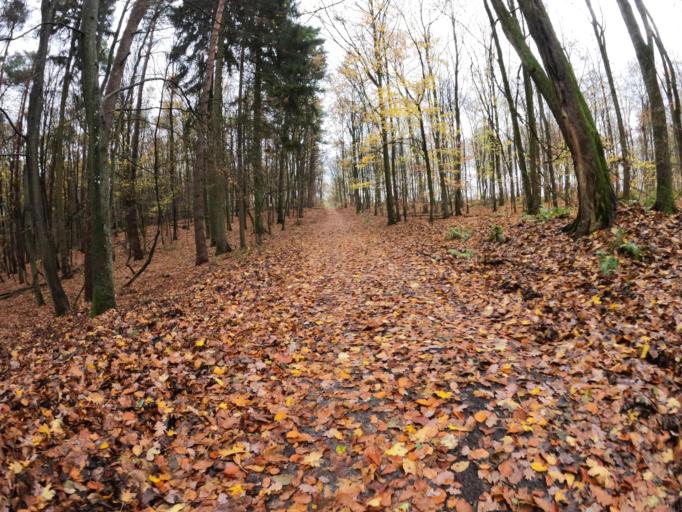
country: PL
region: West Pomeranian Voivodeship
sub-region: Powiat walecki
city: Tuczno
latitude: 53.2416
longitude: 16.2218
